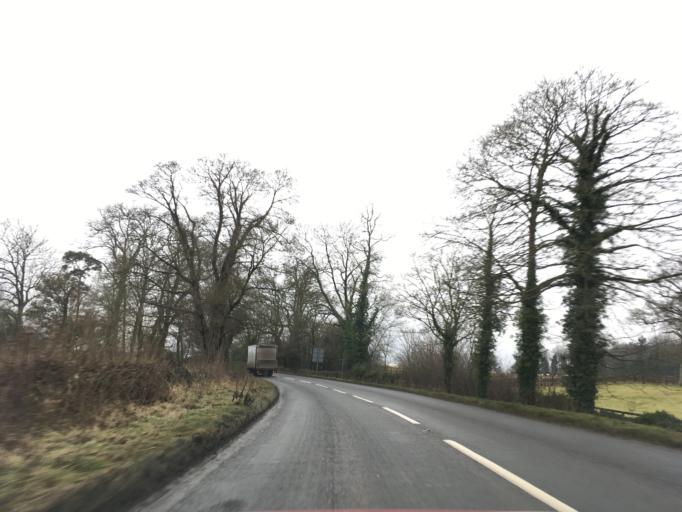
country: GB
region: England
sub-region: Gloucestershire
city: Tetbury
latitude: 51.6662
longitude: -2.1085
